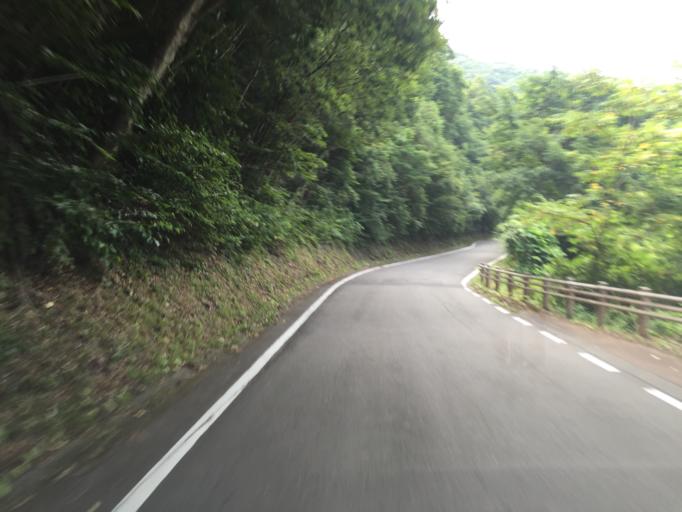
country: JP
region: Fukushima
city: Inawashiro
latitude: 37.4161
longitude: 140.1030
